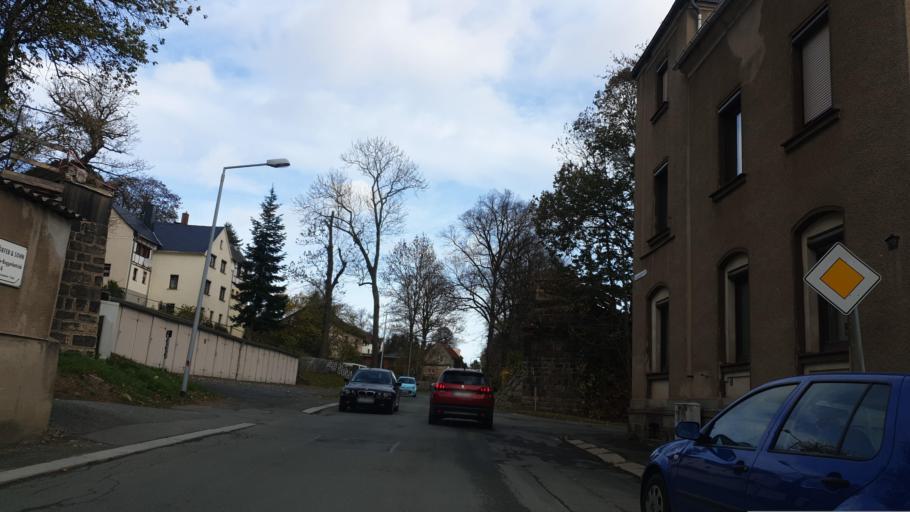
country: DE
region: Saxony
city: Reichenbach/Vogtland
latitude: 50.6295
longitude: 12.3237
